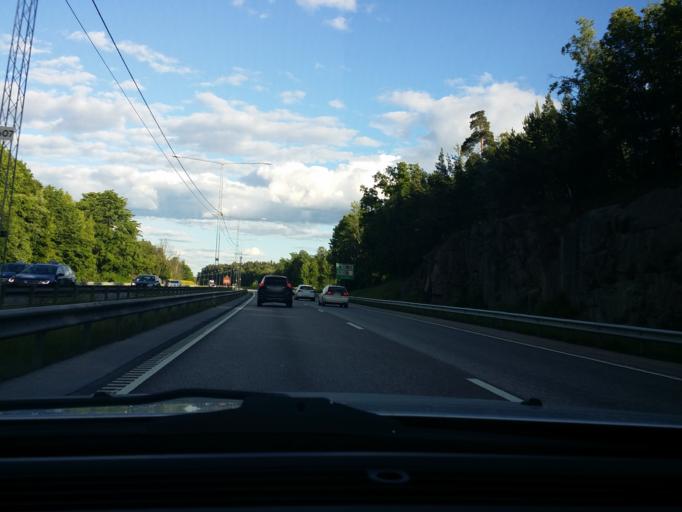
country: SE
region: Stockholm
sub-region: Upplands Vasby Kommun
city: Upplands Vaesby
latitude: 59.5397
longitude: 17.9071
